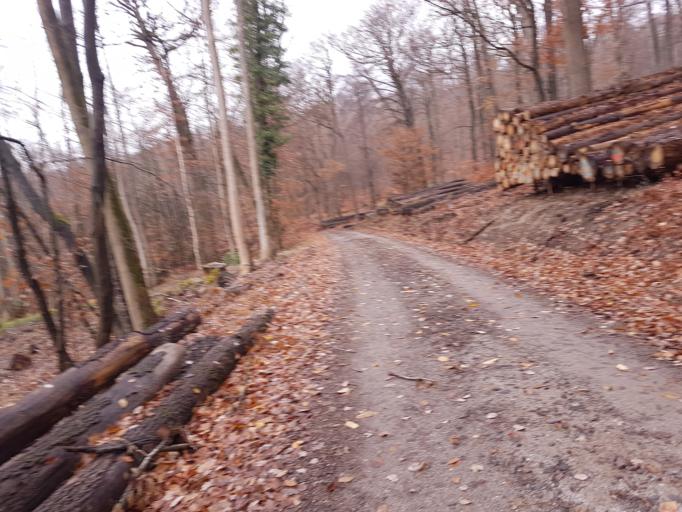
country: DE
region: Hesse
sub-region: Regierungsbezirk Darmstadt
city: Kiedrich
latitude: 50.0550
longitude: 8.0394
